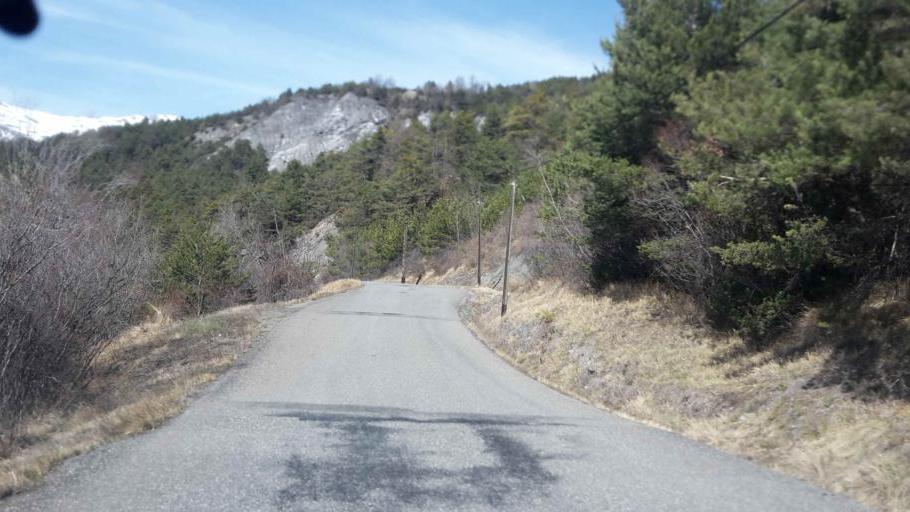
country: FR
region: Provence-Alpes-Cote d'Azur
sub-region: Departement des Hautes-Alpes
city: Embrun
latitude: 44.5655
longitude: 6.5465
